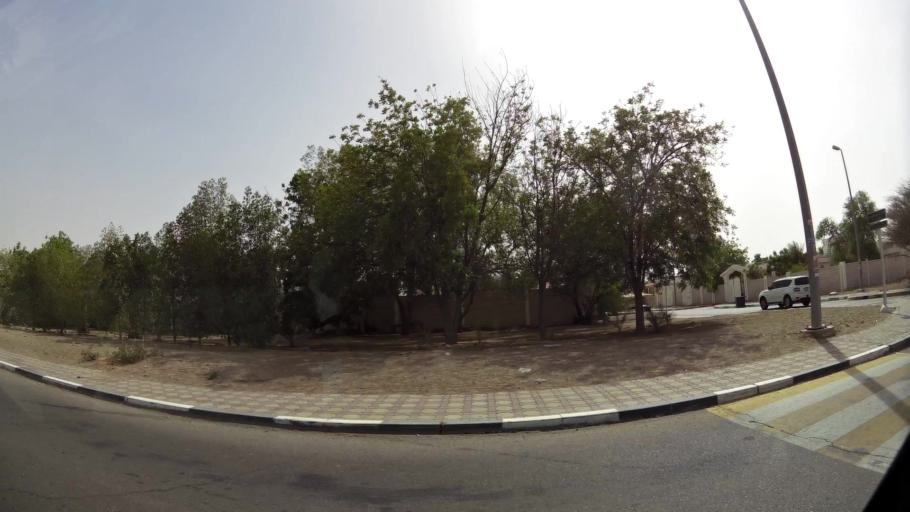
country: AE
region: Abu Dhabi
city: Al Ain
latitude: 24.1795
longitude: 55.6098
